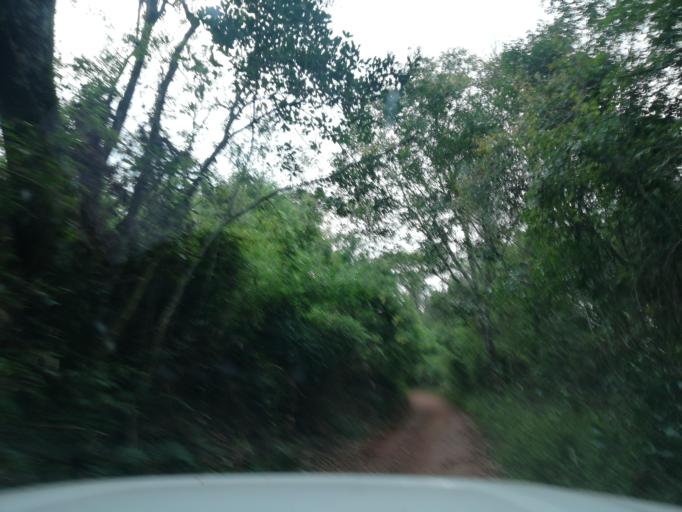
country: AR
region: Misiones
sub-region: Departamento de San Pedro
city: San Pedro
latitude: -26.6320
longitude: -54.0957
